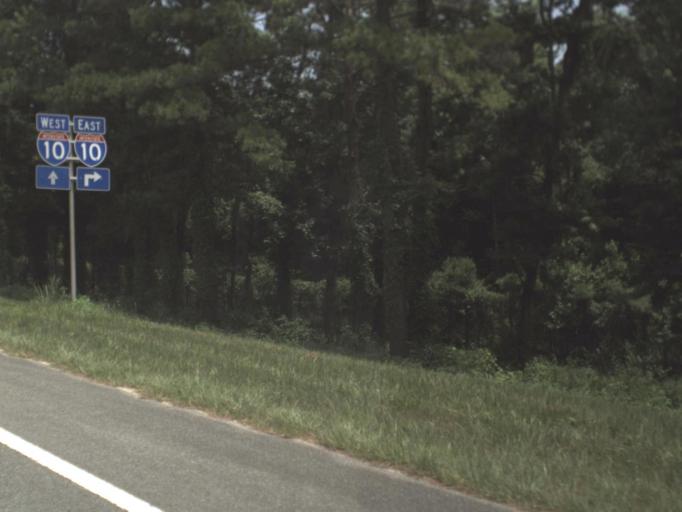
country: US
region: Florida
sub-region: Madison County
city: Madison
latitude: 30.4287
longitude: -83.4579
